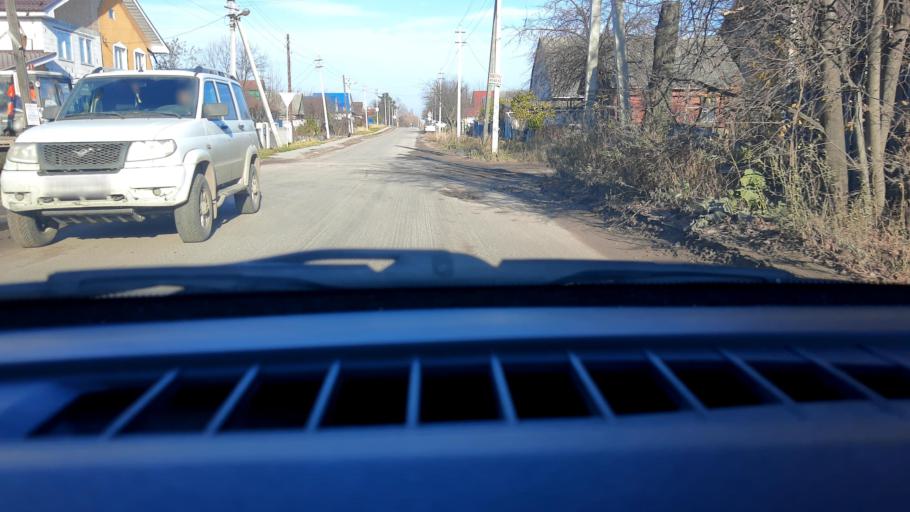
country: RU
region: Nizjnij Novgorod
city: Neklyudovo
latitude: 56.4113
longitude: 43.9800
